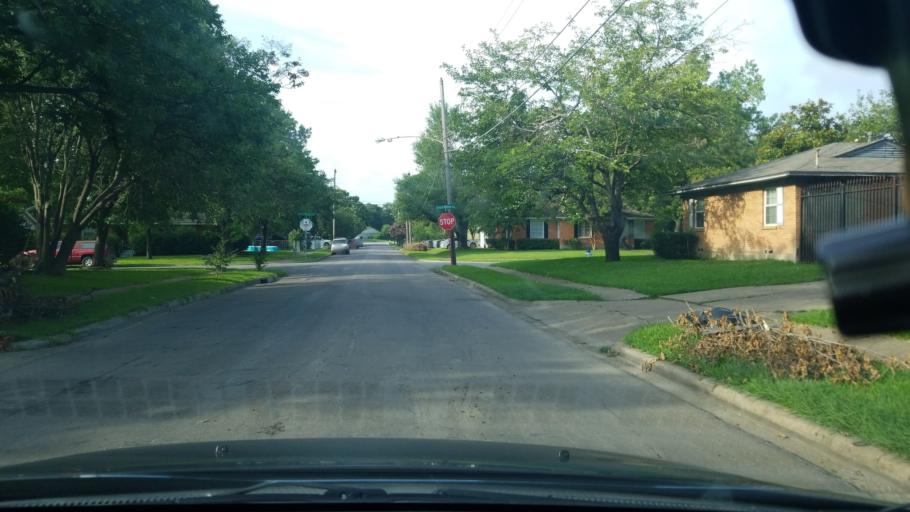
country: US
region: Texas
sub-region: Dallas County
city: Garland
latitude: 32.8291
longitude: -96.6606
